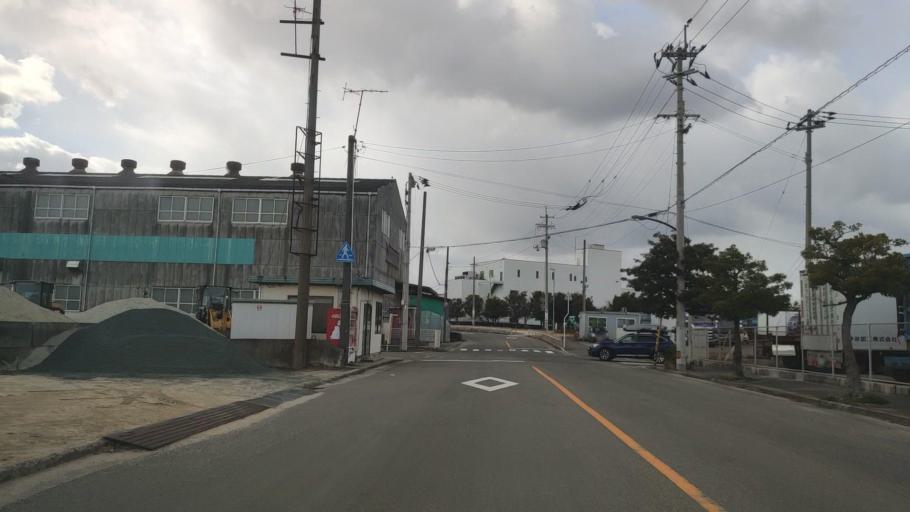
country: JP
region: Ehime
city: Saijo
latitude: 34.0606
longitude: 133.0188
